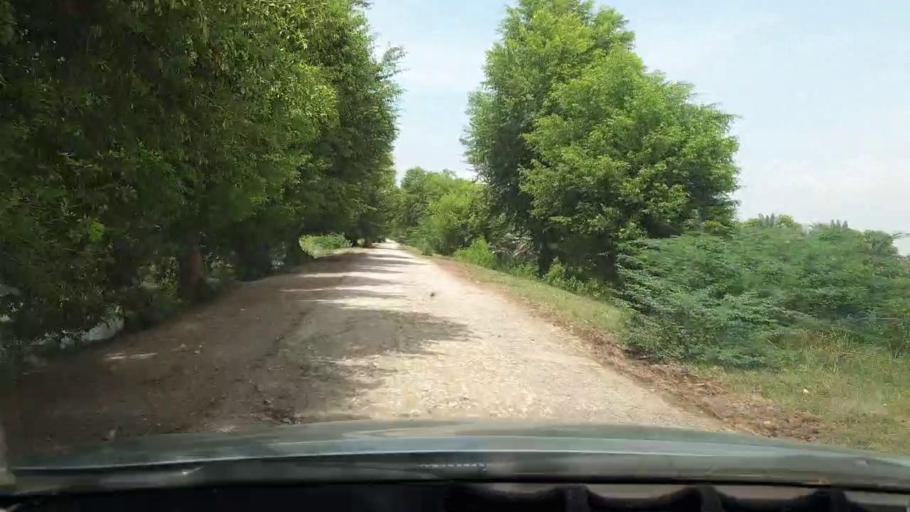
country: PK
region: Sindh
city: Khairpur
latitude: 27.4660
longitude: 68.8050
